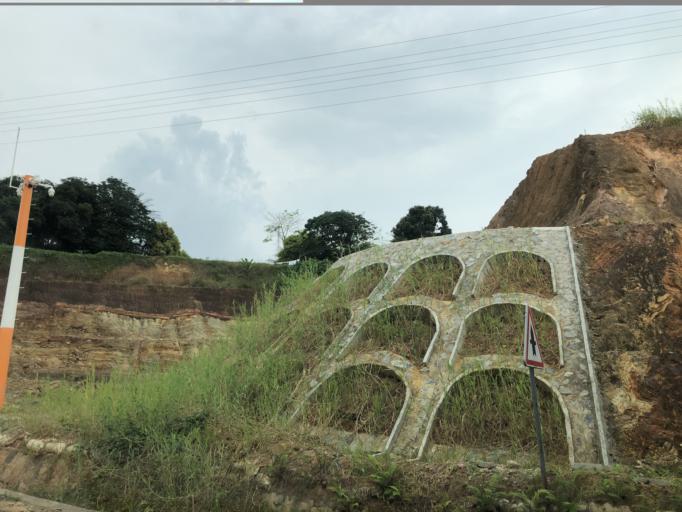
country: CM
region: South Province
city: Kribi
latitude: 2.7238
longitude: 9.8679
